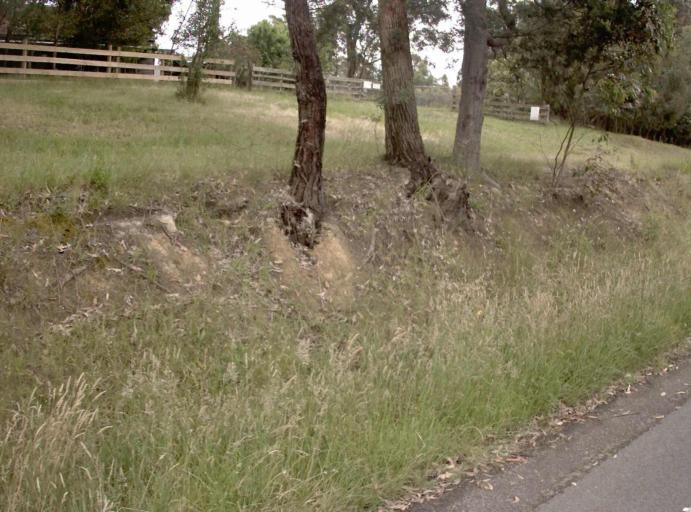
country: AU
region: Victoria
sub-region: Baw Baw
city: Warragul
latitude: -38.0469
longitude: 145.9563
